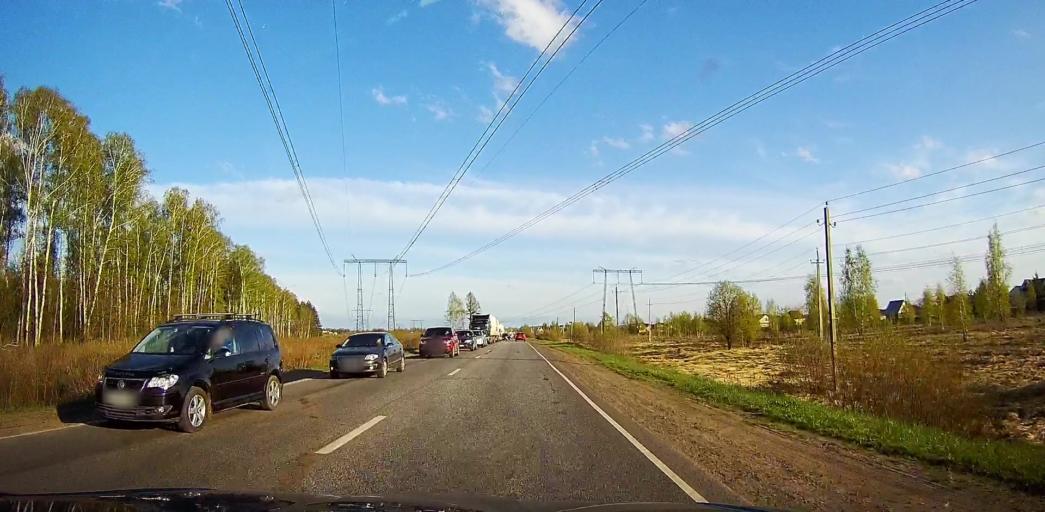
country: RU
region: Moskovskaya
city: Bronnitsy
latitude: 55.3748
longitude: 38.2125
